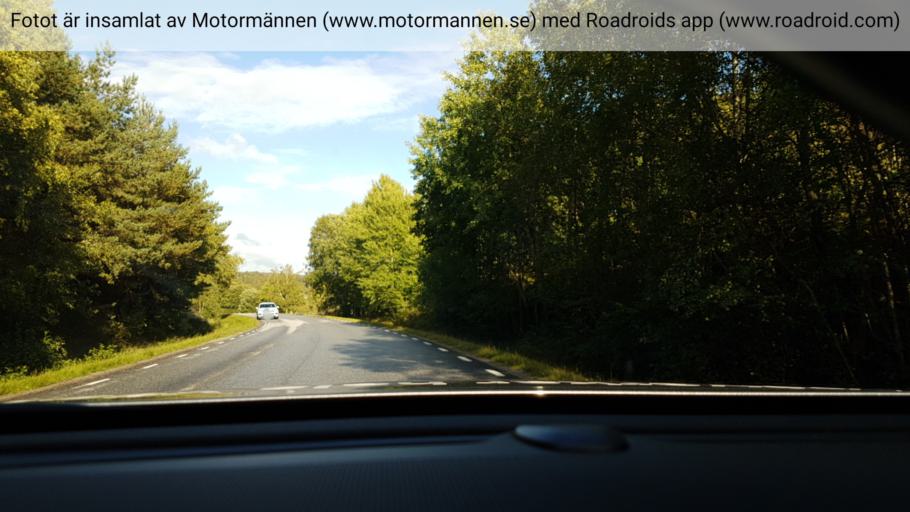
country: SE
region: Vaestra Goetaland
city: Svanesund
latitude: 58.1390
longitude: 11.7796
